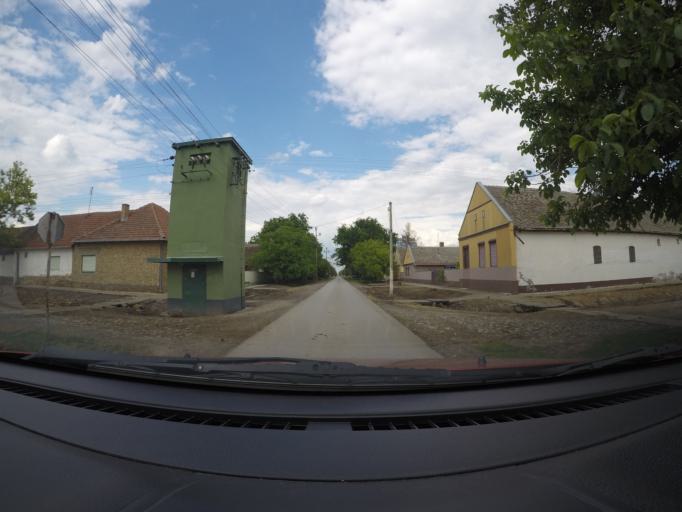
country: RS
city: Begejci
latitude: 45.5038
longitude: 20.6059
